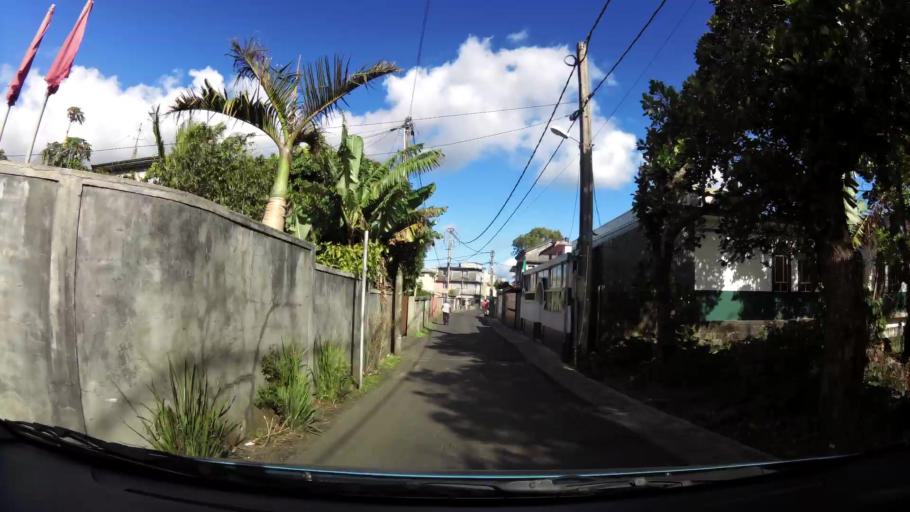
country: MU
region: Plaines Wilhems
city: Curepipe
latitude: -20.3008
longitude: 57.5152
